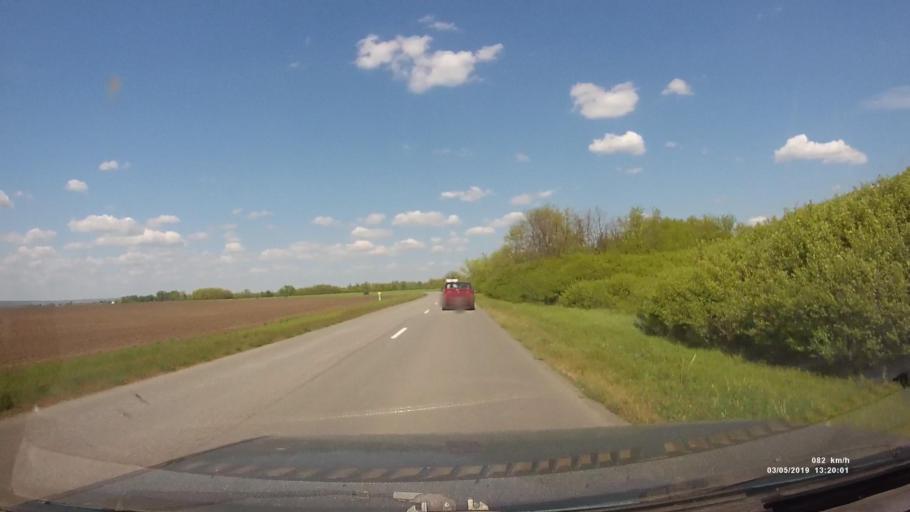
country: RU
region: Rostov
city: Semikarakorsk
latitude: 47.5409
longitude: 40.7526
